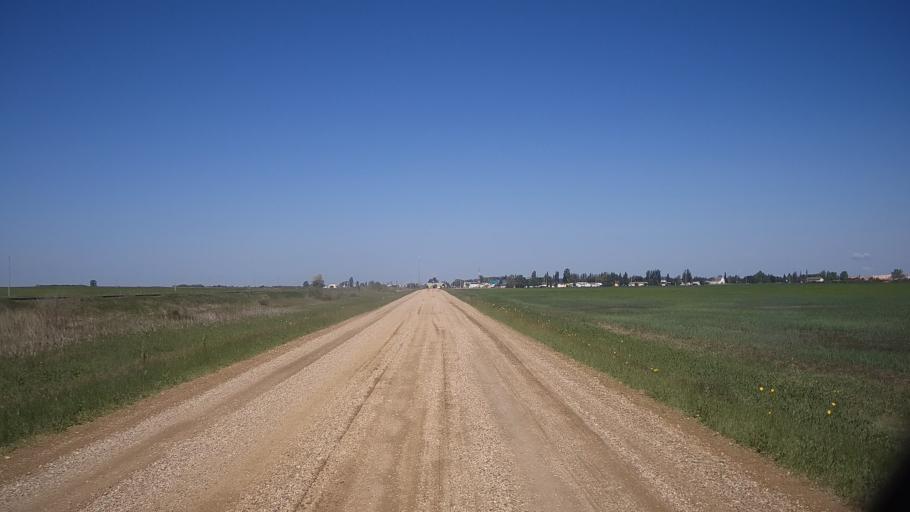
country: CA
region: Saskatchewan
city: Watrous
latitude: 51.8875
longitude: -106.0412
